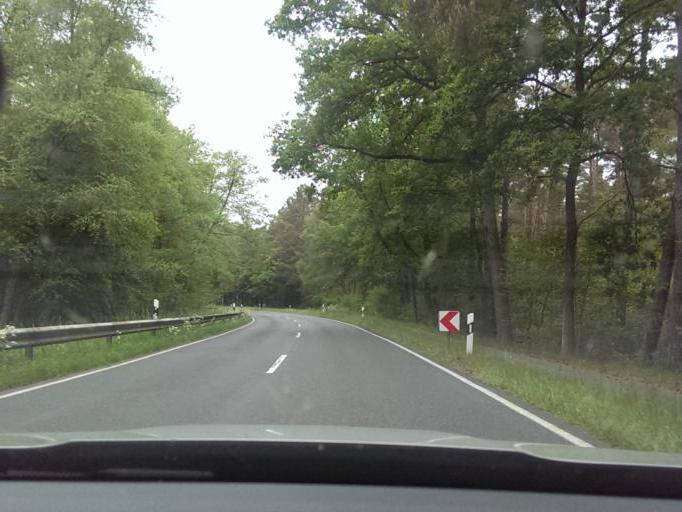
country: DE
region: Lower Saxony
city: Essel
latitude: 52.6889
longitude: 9.7285
